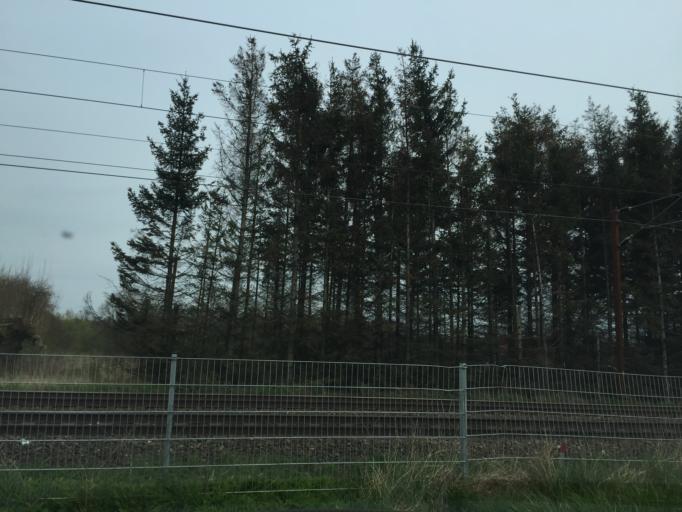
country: DK
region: South Denmark
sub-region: Odense Kommune
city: Neder Holluf
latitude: 55.3894
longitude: 10.4559
